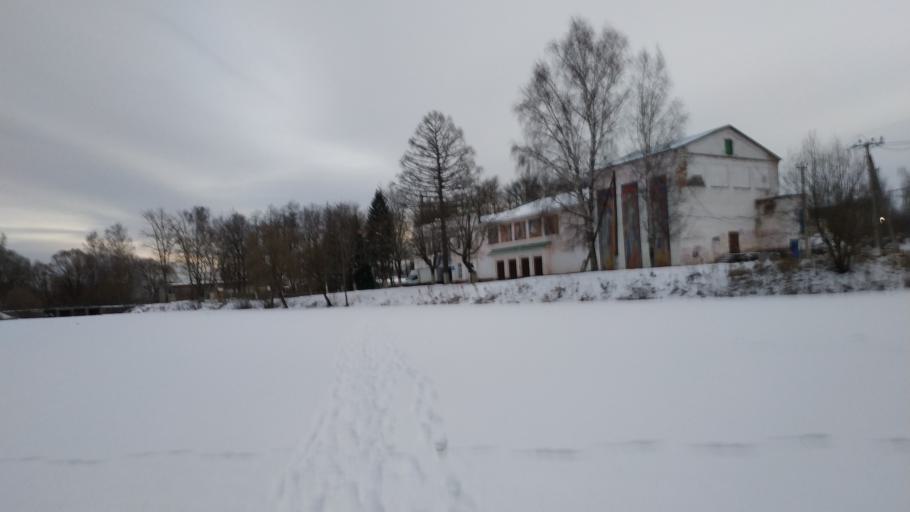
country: RU
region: Vladimir
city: Strunino
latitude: 56.3705
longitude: 38.5867
